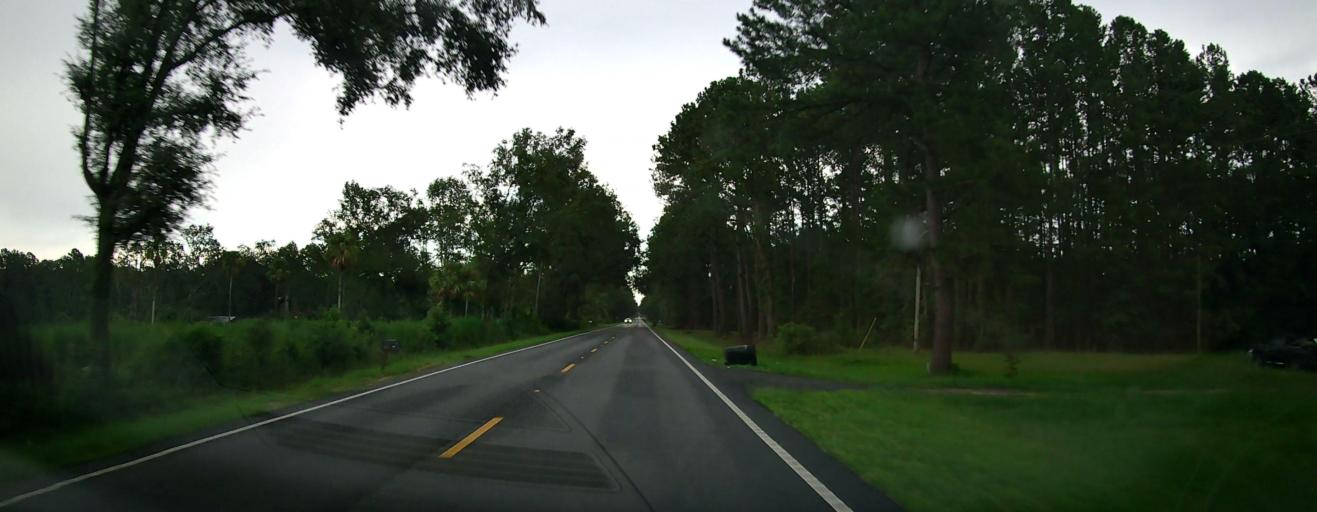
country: US
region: Georgia
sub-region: Glynn County
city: Dock Junction
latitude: 31.2872
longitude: -81.6799
